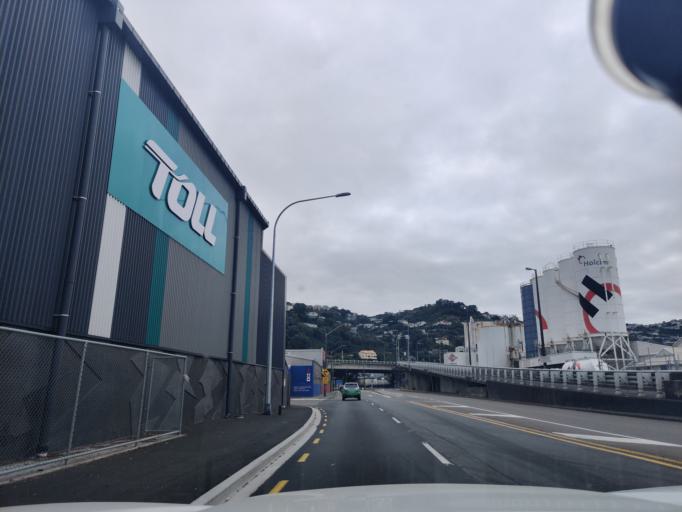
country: NZ
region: Wellington
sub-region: Wellington City
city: Wellington
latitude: -41.2679
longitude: 174.7857
